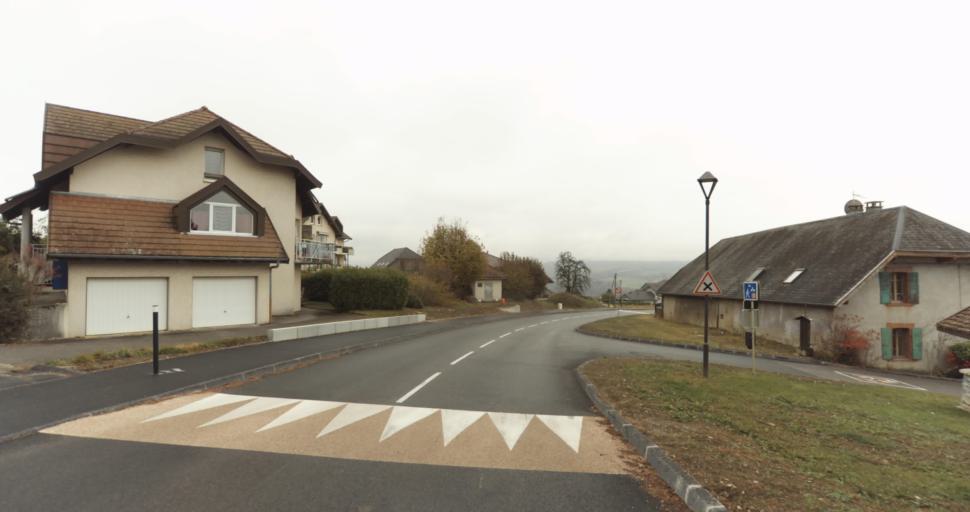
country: FR
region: Rhone-Alpes
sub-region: Departement de la Haute-Savoie
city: Groisy
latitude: 46.0165
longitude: 6.1714
